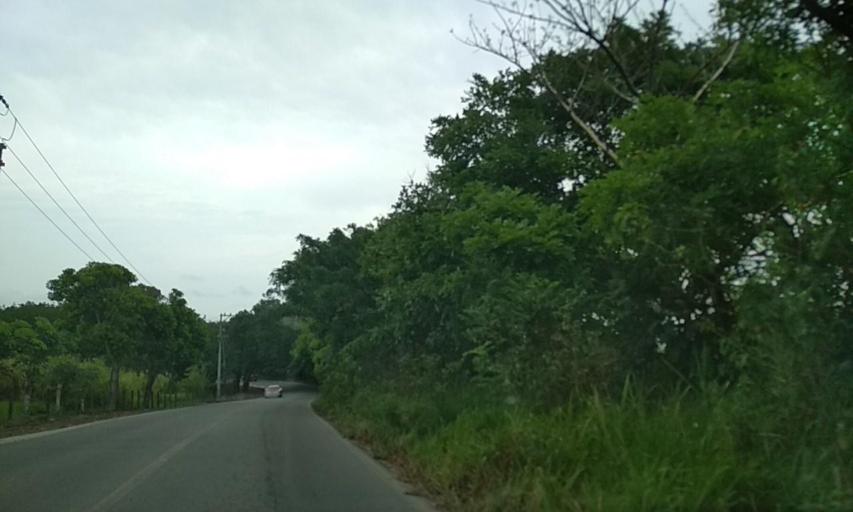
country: MX
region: Veracruz
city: Las Choapas
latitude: 17.8629
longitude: -94.0988
